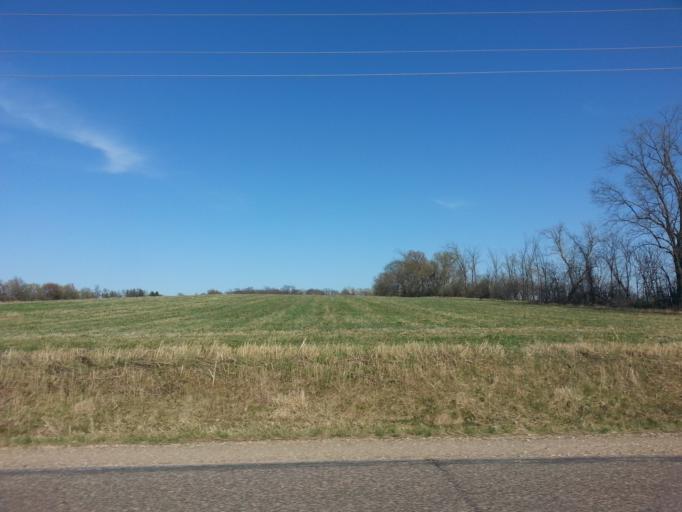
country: US
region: Wisconsin
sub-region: Pierce County
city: River Falls
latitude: 44.7871
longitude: -92.5785
